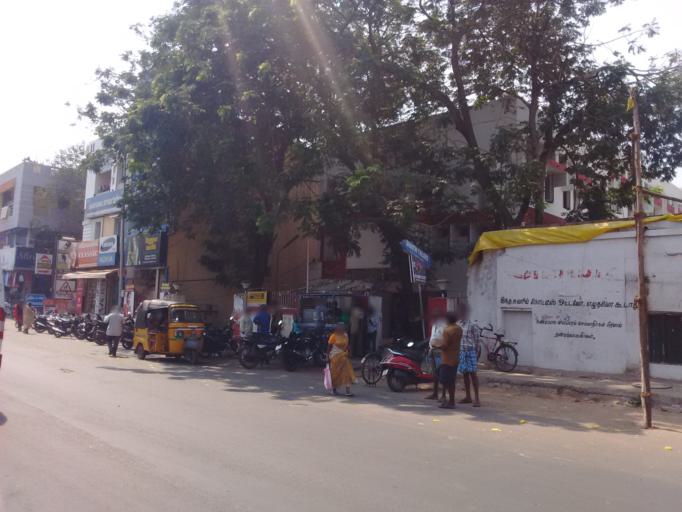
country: IN
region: Tamil Nadu
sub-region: Thiruvallur
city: Tiruvottiyur
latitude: 13.1598
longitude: 80.3024
